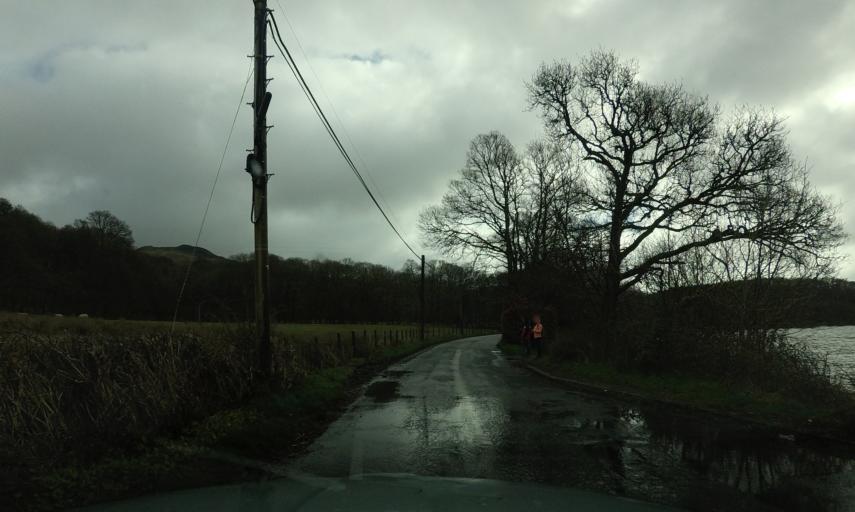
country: GB
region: Scotland
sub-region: West Dunbartonshire
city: Balloch
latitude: 56.0991
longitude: -4.5575
